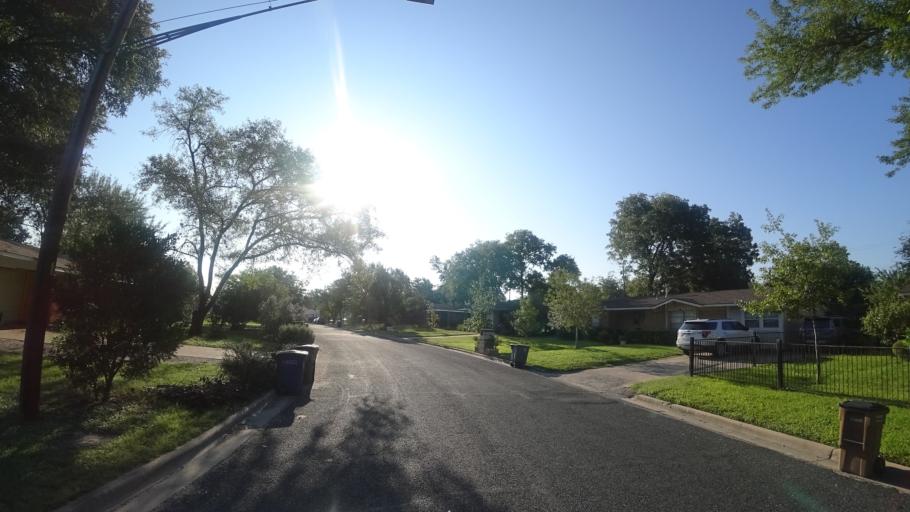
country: US
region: Texas
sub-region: Travis County
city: Austin
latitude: 30.3114
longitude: -97.6832
